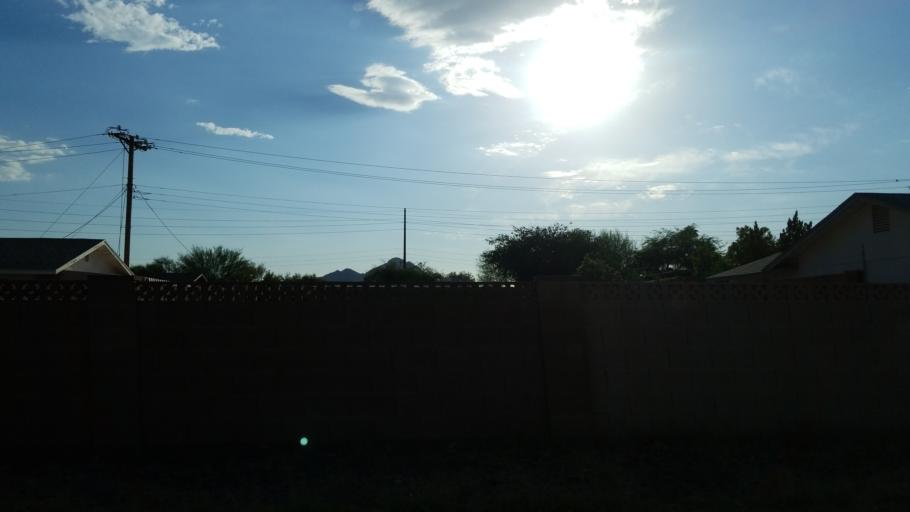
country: US
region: Arizona
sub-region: Maricopa County
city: Scottsdale
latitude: 33.5143
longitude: -111.9046
